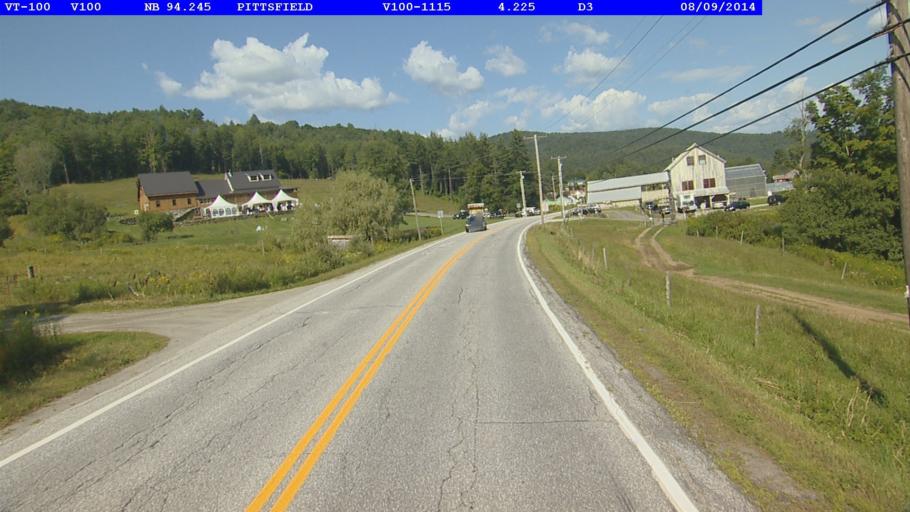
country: US
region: Vermont
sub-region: Orange County
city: Randolph
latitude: 43.7758
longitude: -72.8104
